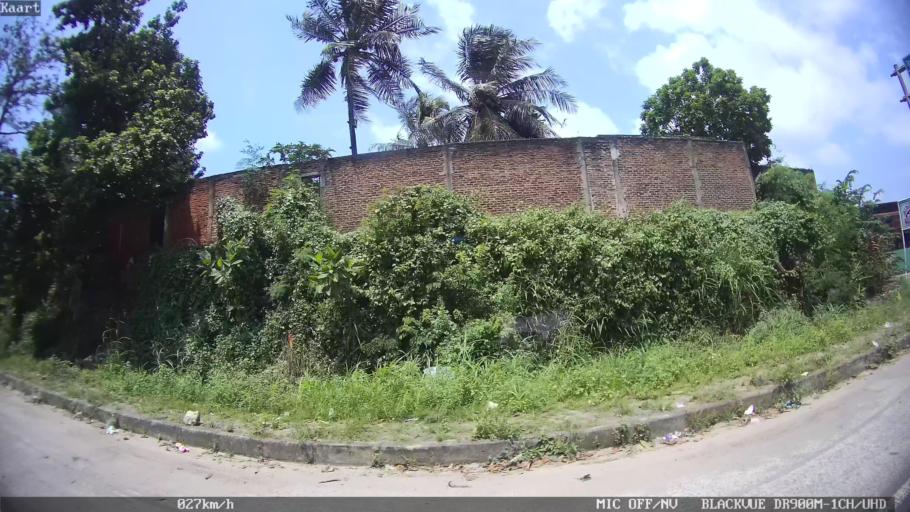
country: ID
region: Lampung
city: Kedaton
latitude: -5.3727
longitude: 105.2764
